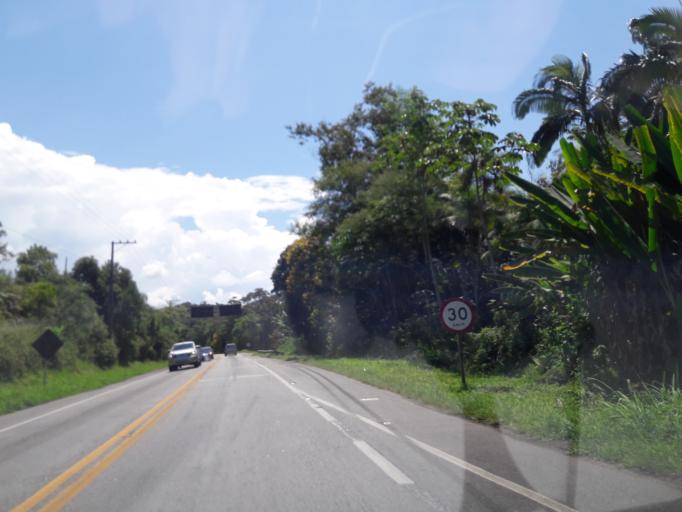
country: BR
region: Parana
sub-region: Antonina
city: Antonina
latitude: -25.5228
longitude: -48.7961
